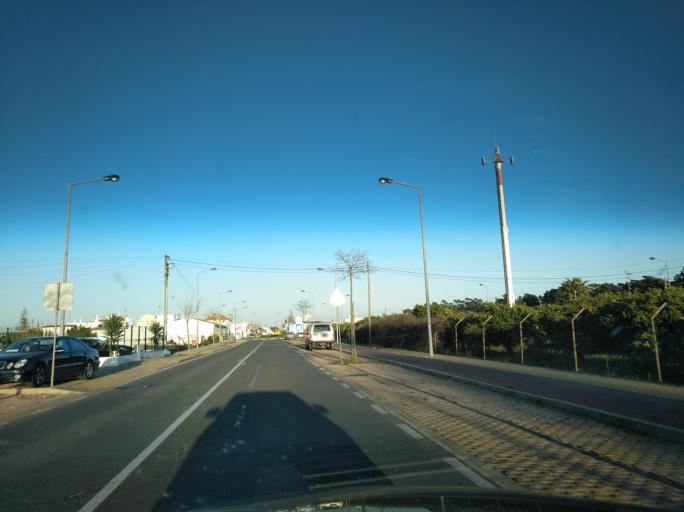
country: PT
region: Faro
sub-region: Vila Real de Santo Antonio
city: Monte Gordo
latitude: 37.1898
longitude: -7.4388
